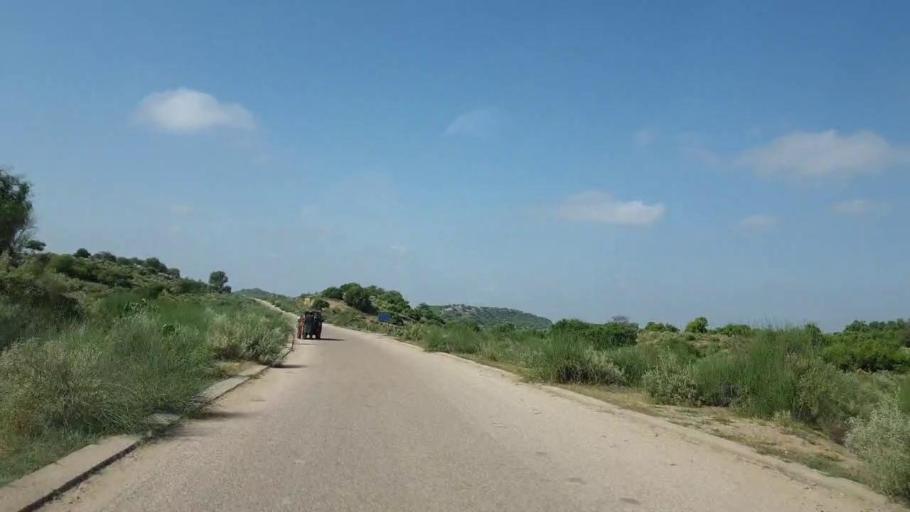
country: PK
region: Sindh
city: Mithi
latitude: 24.5576
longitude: 69.8962
